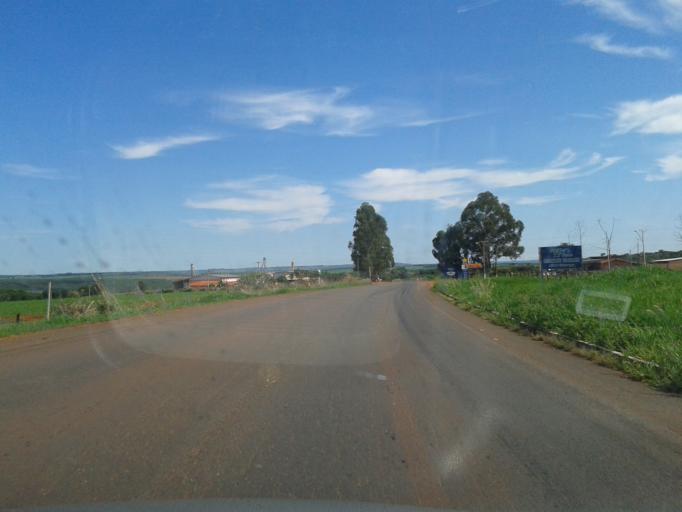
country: BR
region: Goias
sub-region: Piracanjuba
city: Piracanjuba
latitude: -17.1924
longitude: -48.7167
